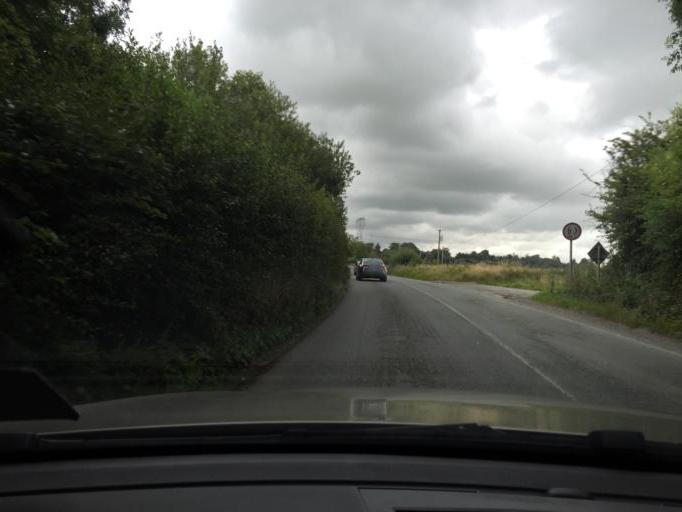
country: IE
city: Confey
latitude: 53.3968
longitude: -6.5343
